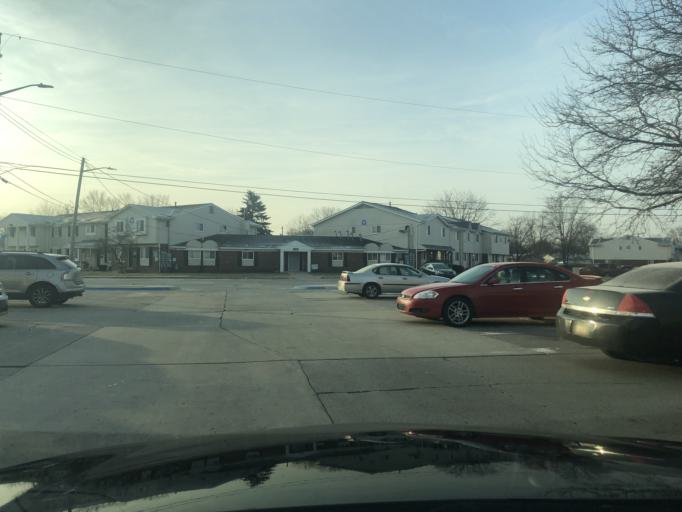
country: US
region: Michigan
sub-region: Wayne County
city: Romulus
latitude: 42.1948
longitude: -83.3340
